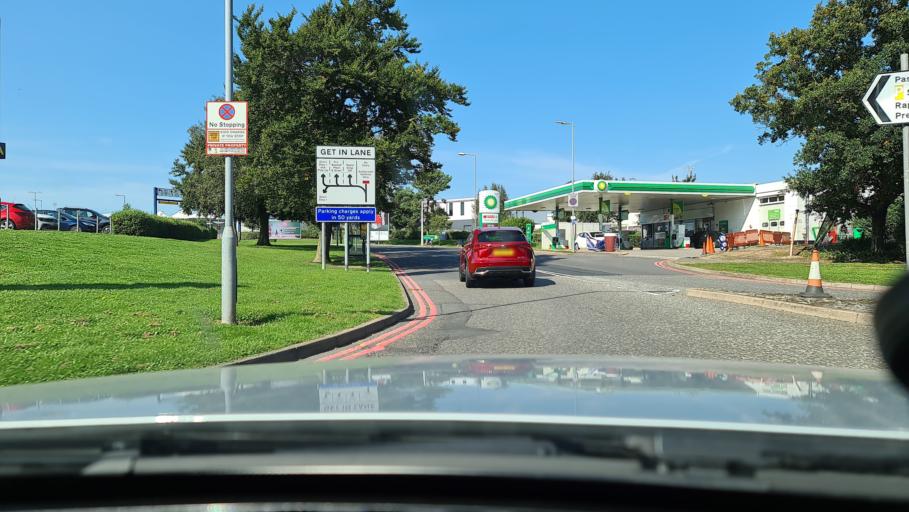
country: GB
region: England
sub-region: Leicestershire
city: Castle Donington
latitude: 52.8255
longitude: -1.3255
